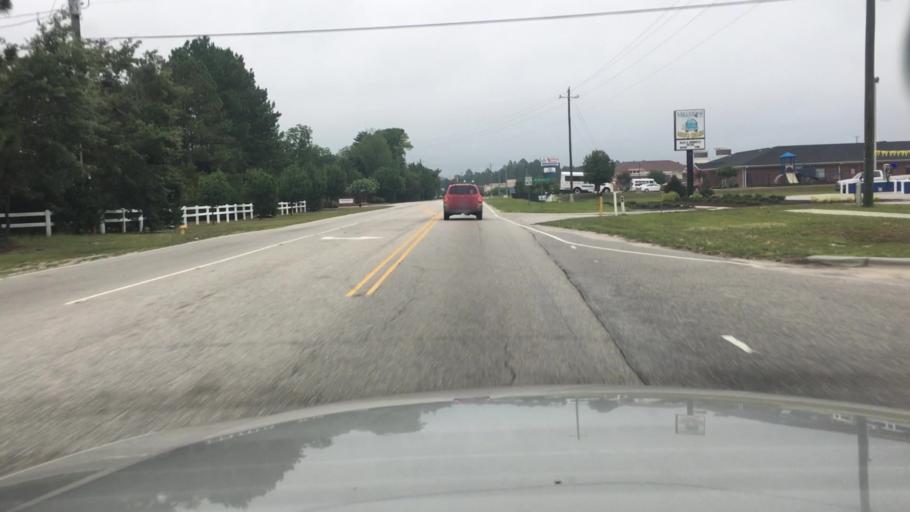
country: US
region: North Carolina
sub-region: Cumberland County
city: Hope Mills
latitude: 34.9797
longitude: -78.9792
